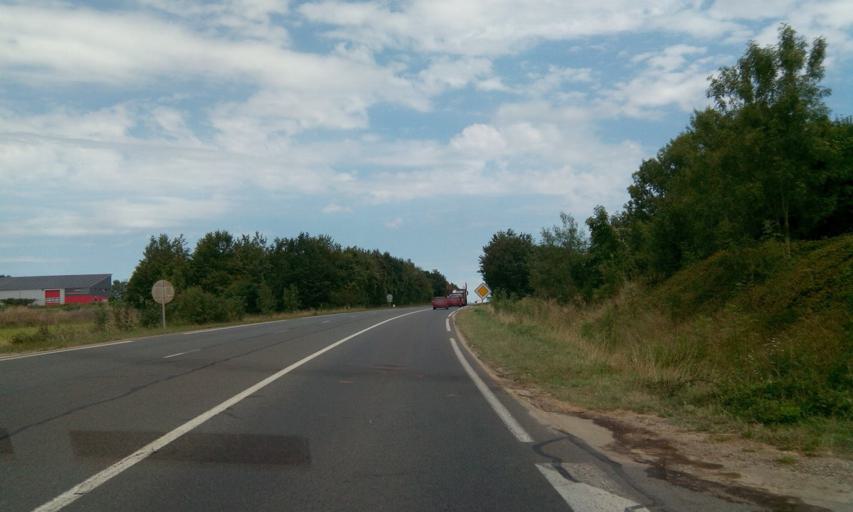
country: FR
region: Poitou-Charentes
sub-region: Departement des Deux-Sevres
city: Melle
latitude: 46.2160
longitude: -0.1574
